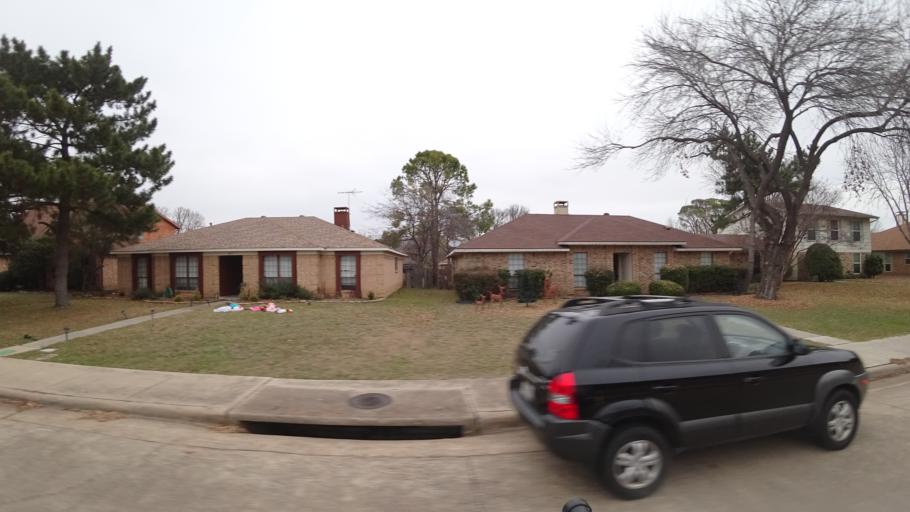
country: US
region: Texas
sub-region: Denton County
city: Highland Village
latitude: 33.0529
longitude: -97.0431
